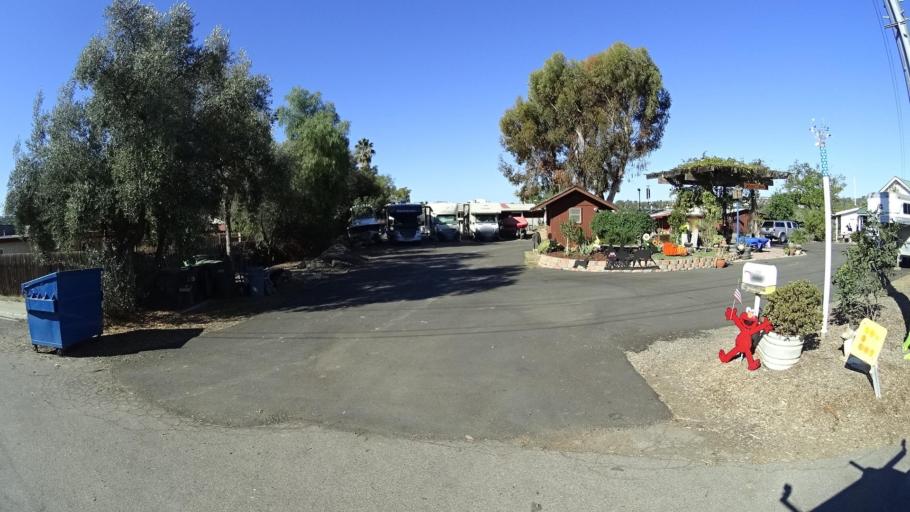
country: US
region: California
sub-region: San Diego County
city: Bonita
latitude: 32.6784
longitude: -117.0083
